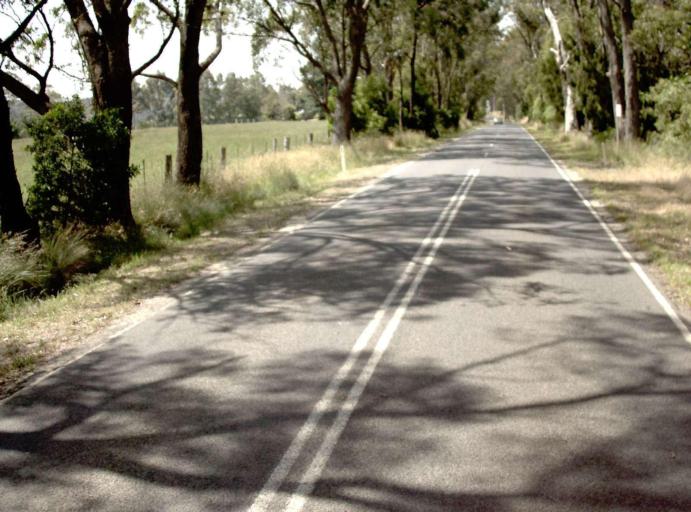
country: AU
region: Victoria
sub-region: Latrobe
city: Traralgon
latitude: -38.2949
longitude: 146.5384
